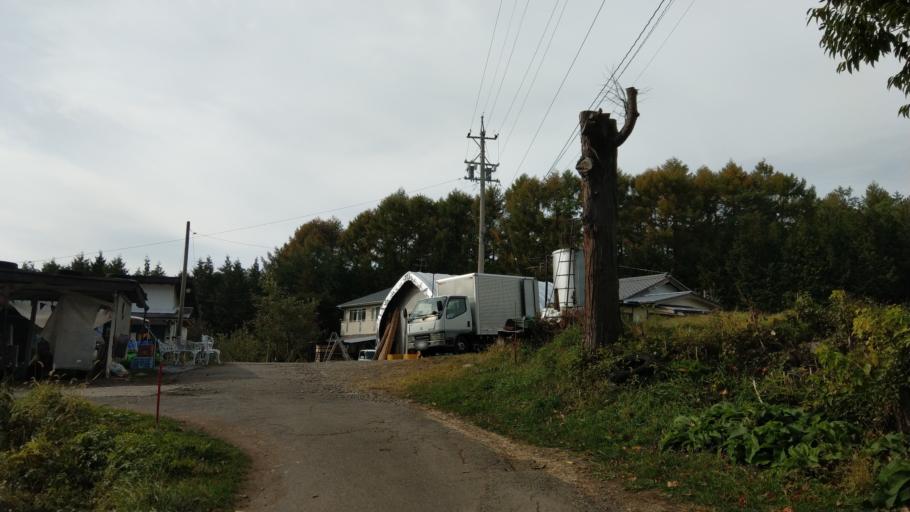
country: JP
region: Nagano
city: Komoro
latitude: 36.3471
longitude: 138.4440
